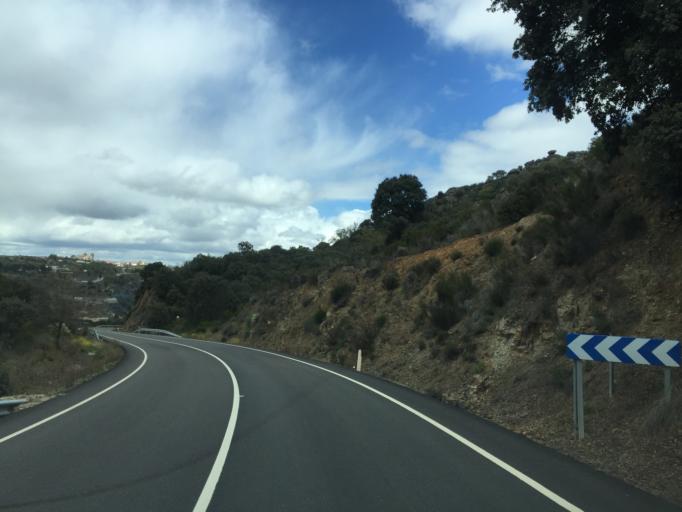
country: PT
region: Braganca
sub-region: Miranda do Douro
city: Miranda do Douro
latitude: 41.4814
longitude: -6.2534
